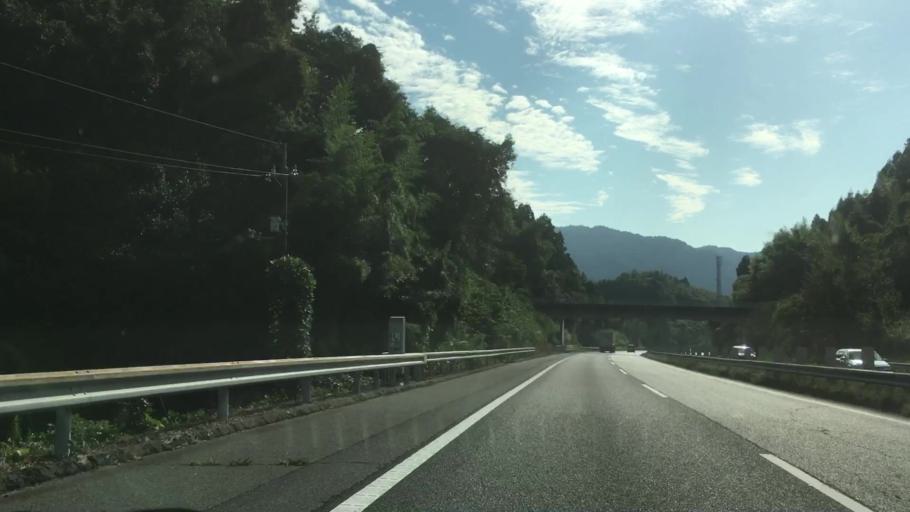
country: JP
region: Yamaguchi
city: Hikari
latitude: 34.0308
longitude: 131.9656
